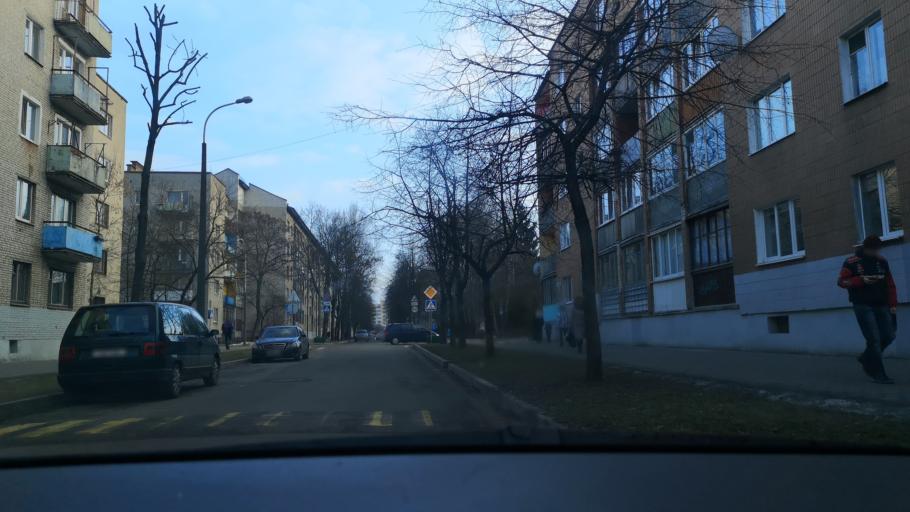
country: BY
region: Brest
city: Brest
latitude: 52.0917
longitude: 23.6983
